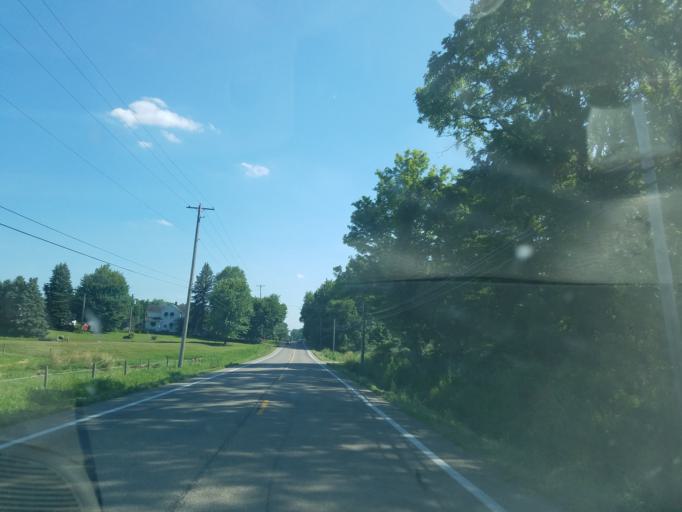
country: US
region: Ohio
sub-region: Portage County
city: Ravenna
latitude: 41.1942
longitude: -81.2463
